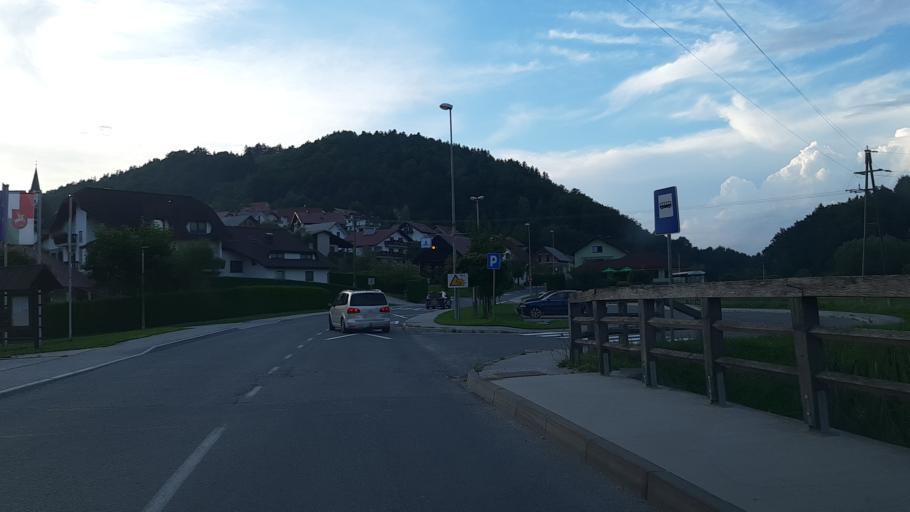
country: SI
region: Sentjur pri Celju
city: Sentjur
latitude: 46.1875
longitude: 15.4302
